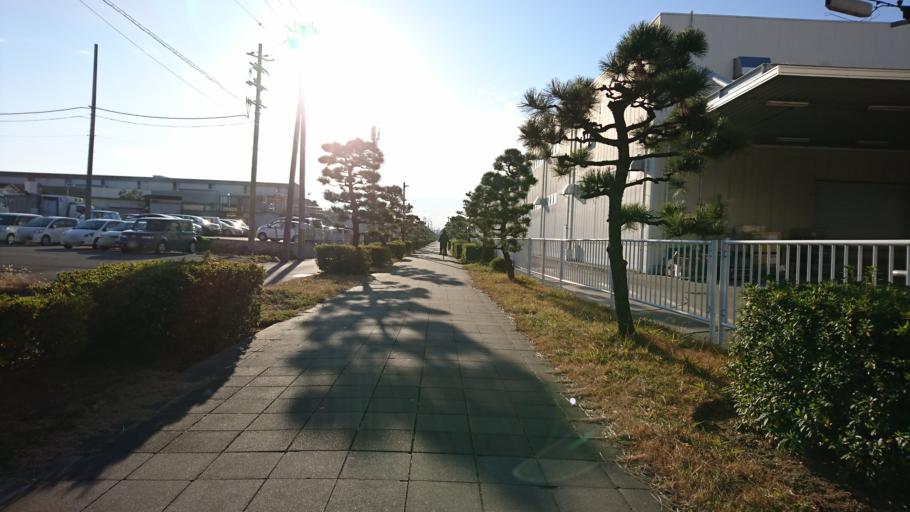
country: JP
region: Hyogo
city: Kakogawacho-honmachi
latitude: 34.7484
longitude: 134.8399
